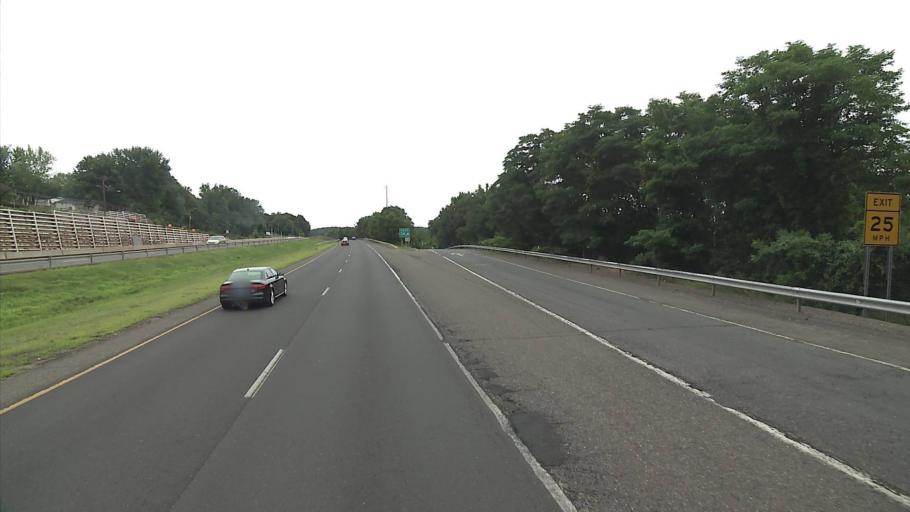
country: US
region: Connecticut
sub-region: New Haven County
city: Waterbury
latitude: 41.5826
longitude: -73.0528
